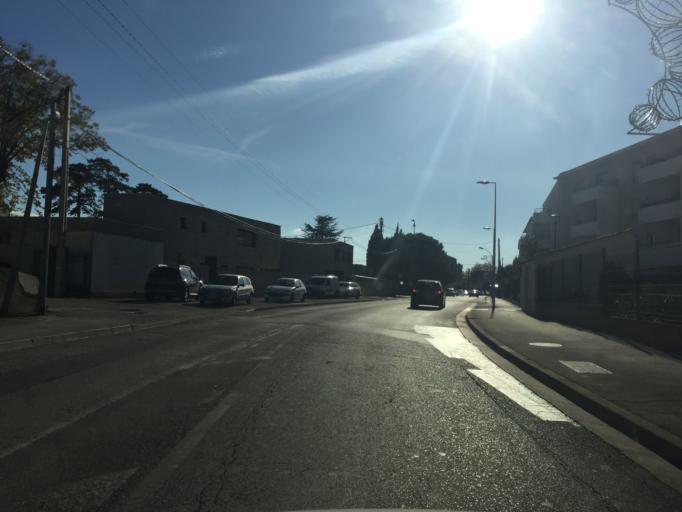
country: FR
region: Provence-Alpes-Cote d'Azur
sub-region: Departement des Bouches-du-Rhone
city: Salon-de-Provence
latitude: 43.6459
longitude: 5.1031
